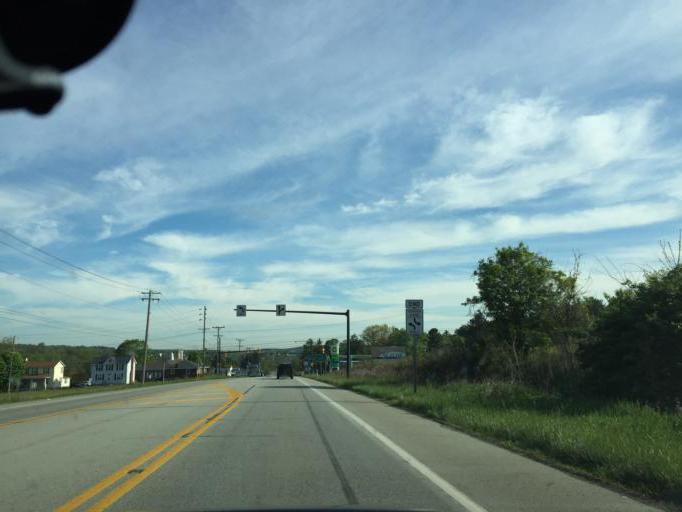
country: US
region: Pennsylvania
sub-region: Westmoreland County
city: Lawson Heights
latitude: 40.2944
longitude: -79.3940
